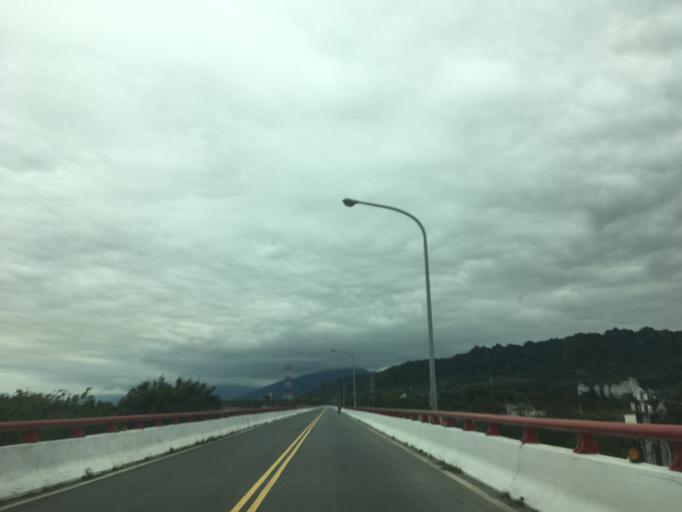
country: TW
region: Taiwan
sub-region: Taitung
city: Taitung
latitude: 22.8108
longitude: 121.1379
